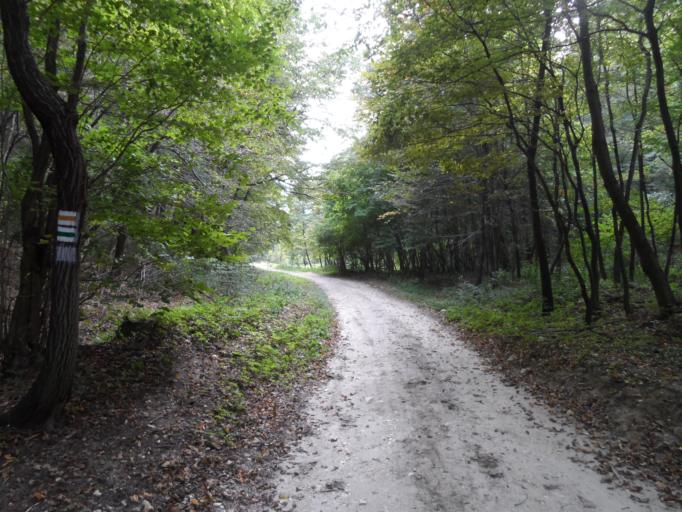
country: HU
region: Veszprem
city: Ajka
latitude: 47.2136
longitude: 17.5635
